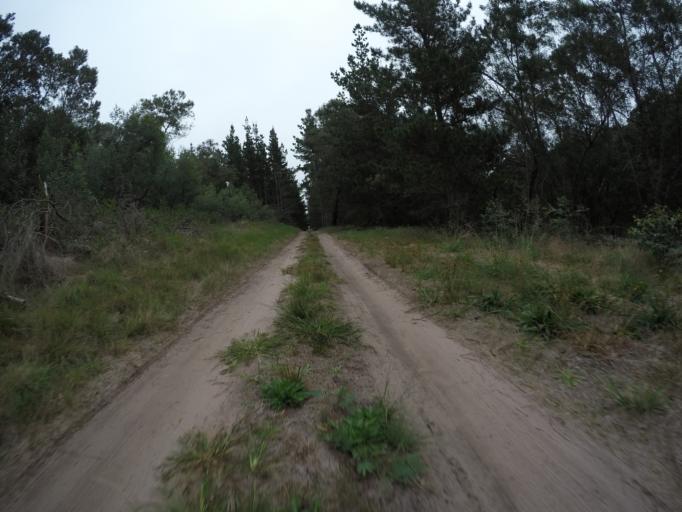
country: ZA
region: Western Cape
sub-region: Eden District Municipality
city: Knysna
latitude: -34.0092
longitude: 22.8088
